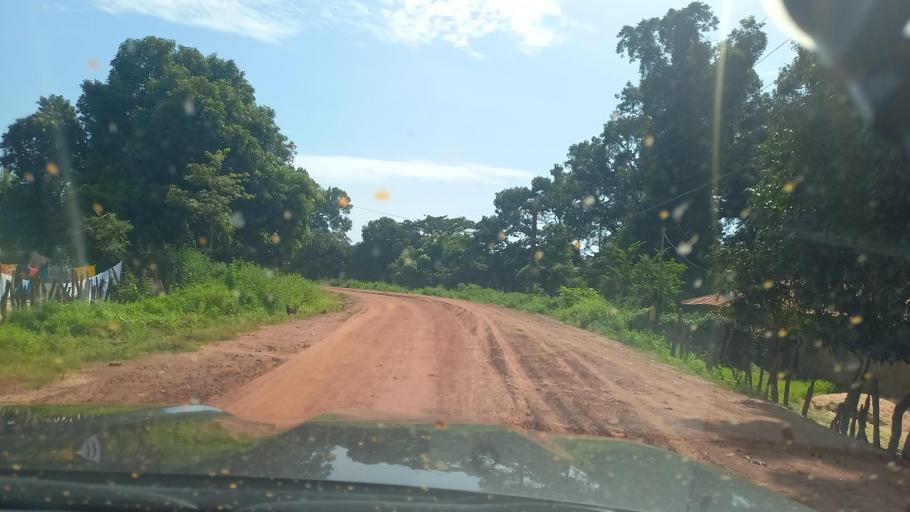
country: SN
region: Ziguinchor
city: Adeane
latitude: 12.6642
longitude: -16.1067
